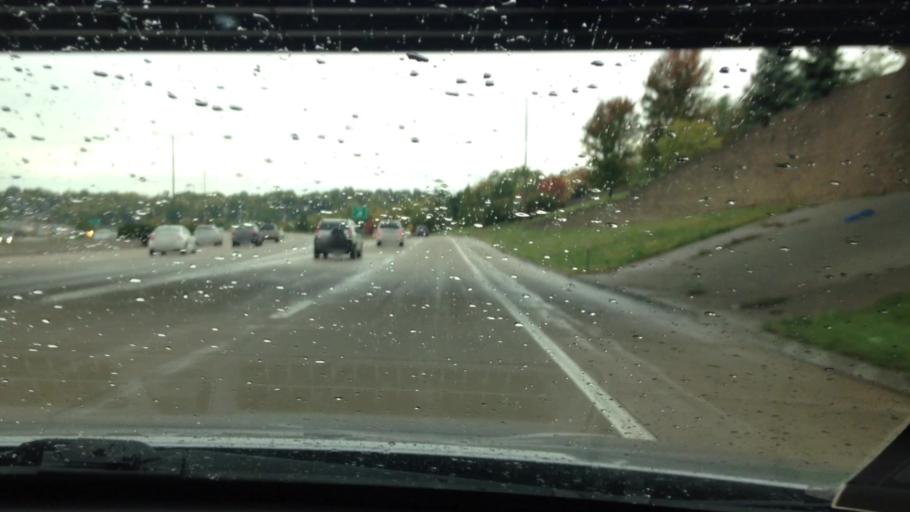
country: US
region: Missouri
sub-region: Jackson County
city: Kansas City
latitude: 39.0487
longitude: -94.5620
